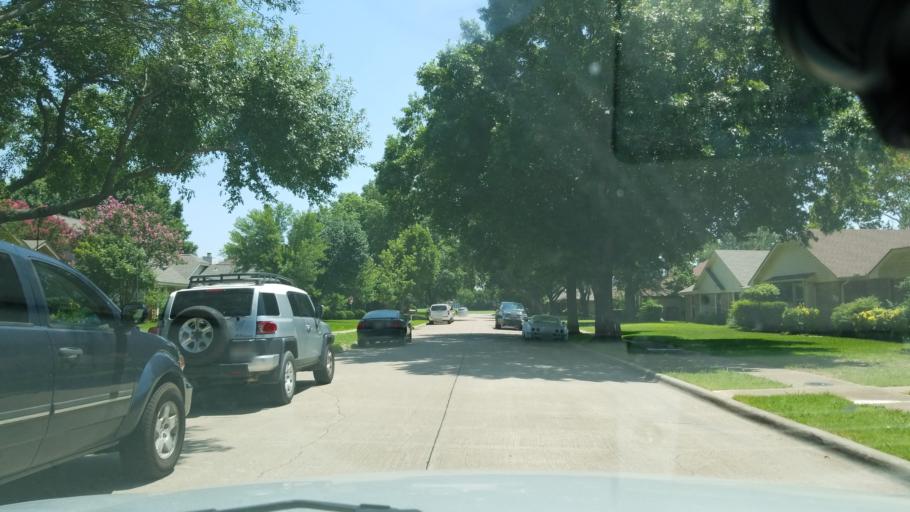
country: US
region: Texas
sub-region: Dallas County
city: Coppell
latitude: 32.9631
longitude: -96.9920
